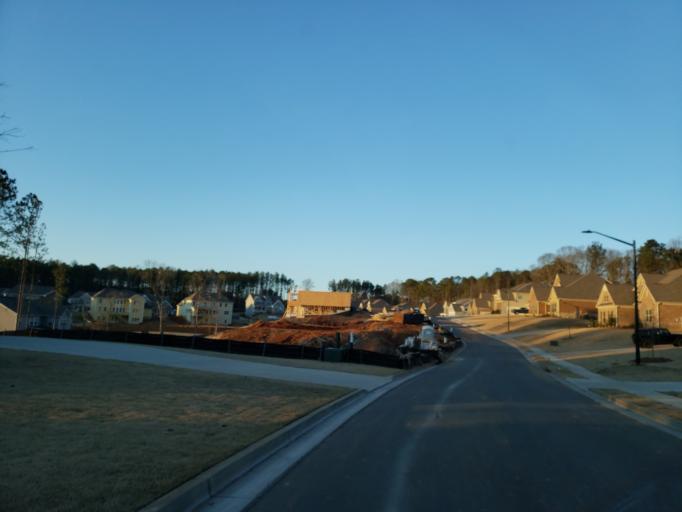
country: US
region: Georgia
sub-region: Cherokee County
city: Woodstock
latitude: 34.1173
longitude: -84.4502
